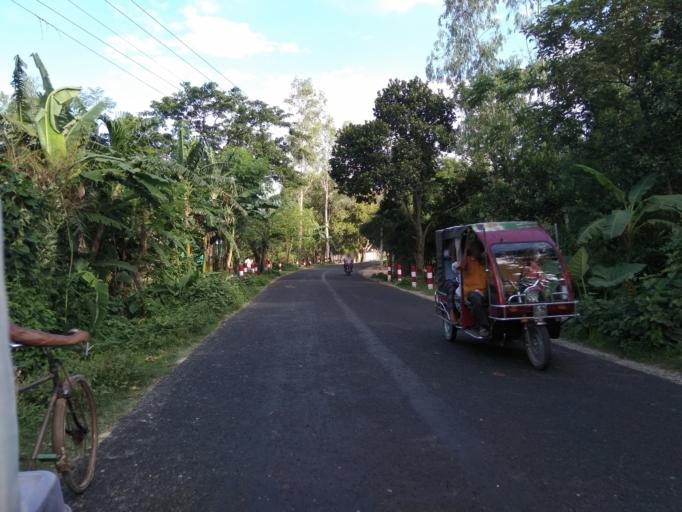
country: BD
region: Rangpur Division
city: Rangpur
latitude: 25.8440
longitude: 89.1125
